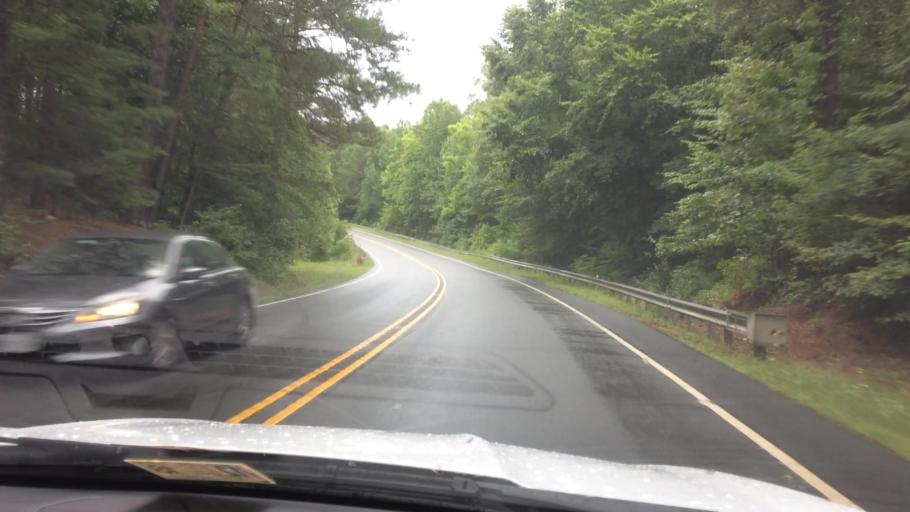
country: US
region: Virginia
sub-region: King William County
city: West Point
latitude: 37.5590
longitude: -76.7454
